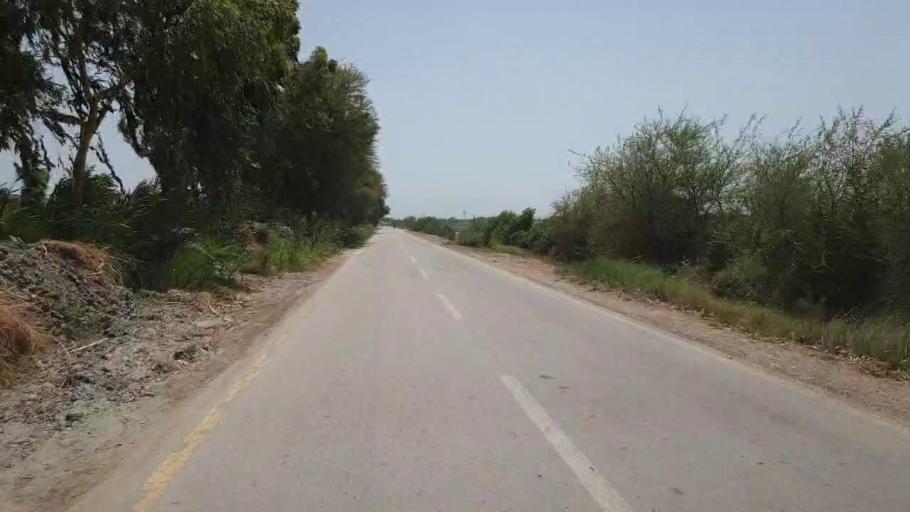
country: PK
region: Sindh
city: Daur
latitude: 26.3518
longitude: 68.1430
